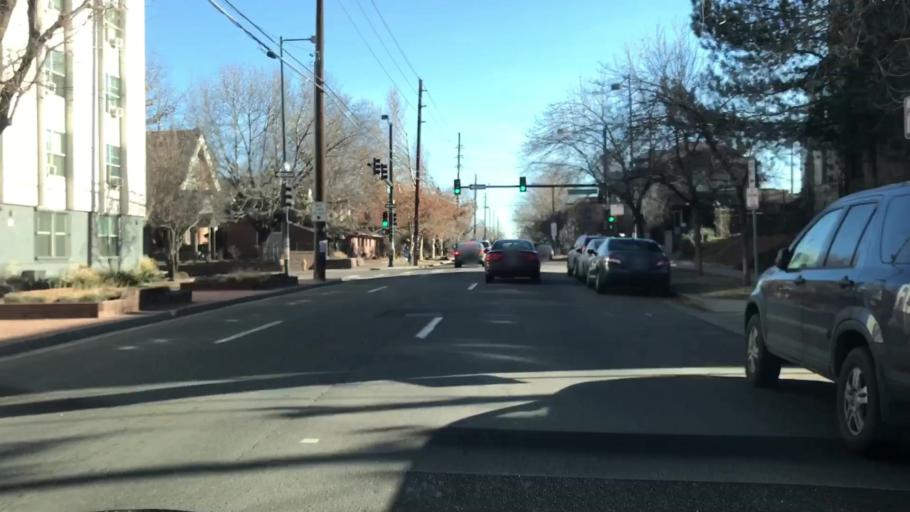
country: US
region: Colorado
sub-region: Denver County
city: Denver
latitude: 39.7384
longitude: -104.9593
